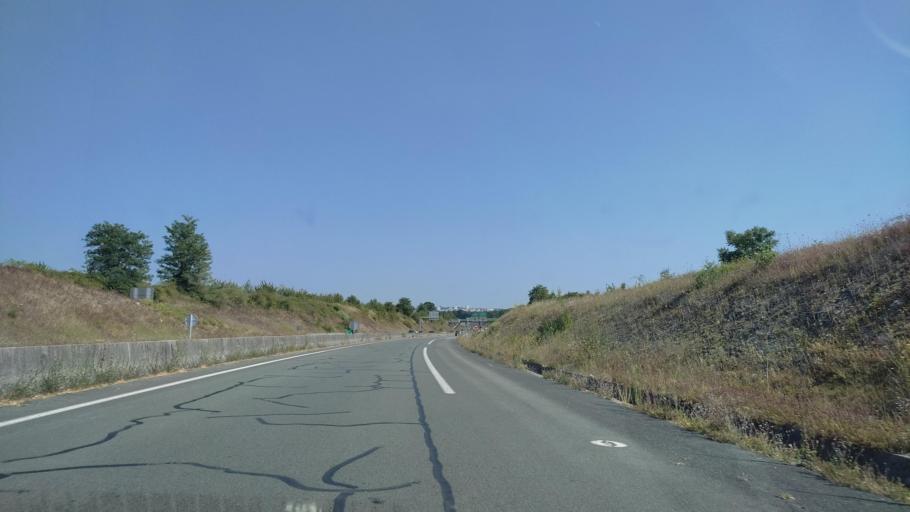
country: FR
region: Poitou-Charentes
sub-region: Departement de la Charente
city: Saint-Yrieix-sur-Charente
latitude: 45.6788
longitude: 0.1331
